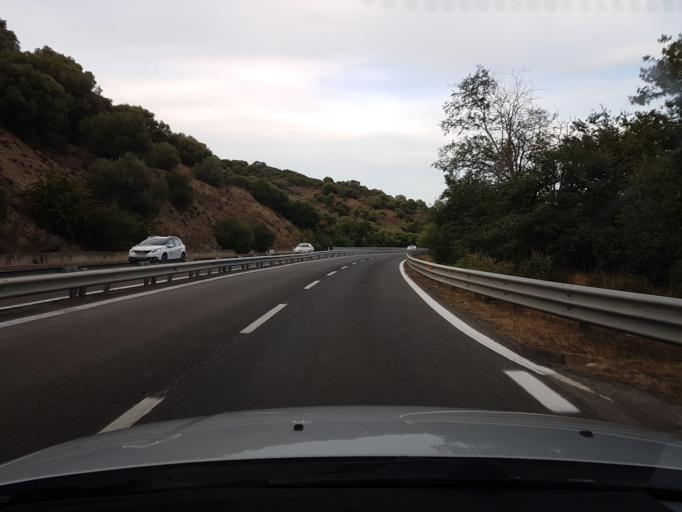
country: IT
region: Sardinia
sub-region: Provincia di Nuoro
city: Orune
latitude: 40.3611
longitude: 9.3544
